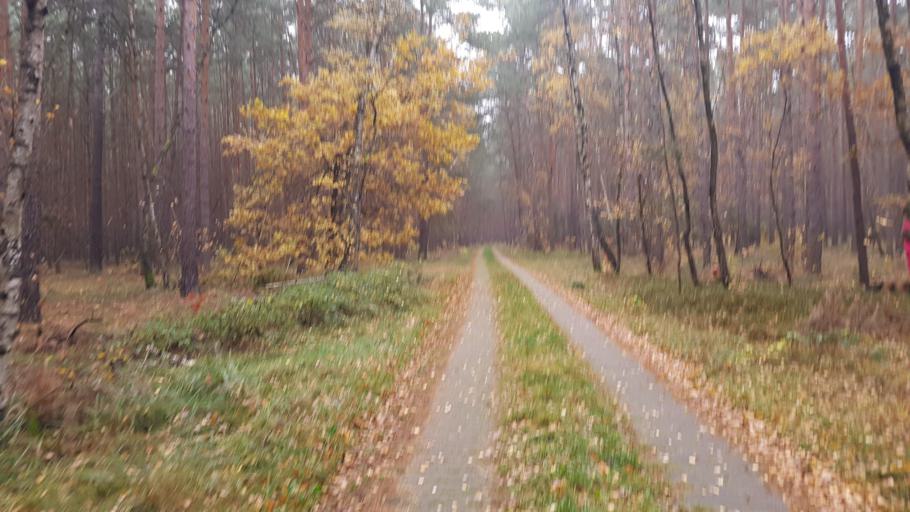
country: DE
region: Brandenburg
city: Merzdorf
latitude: 51.3812
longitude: 13.5247
